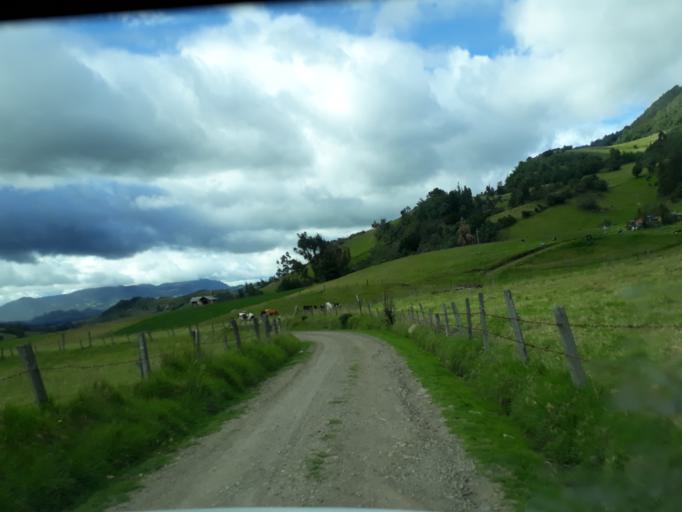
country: CO
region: Cundinamarca
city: La Mesa
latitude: 5.2634
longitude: -73.8999
